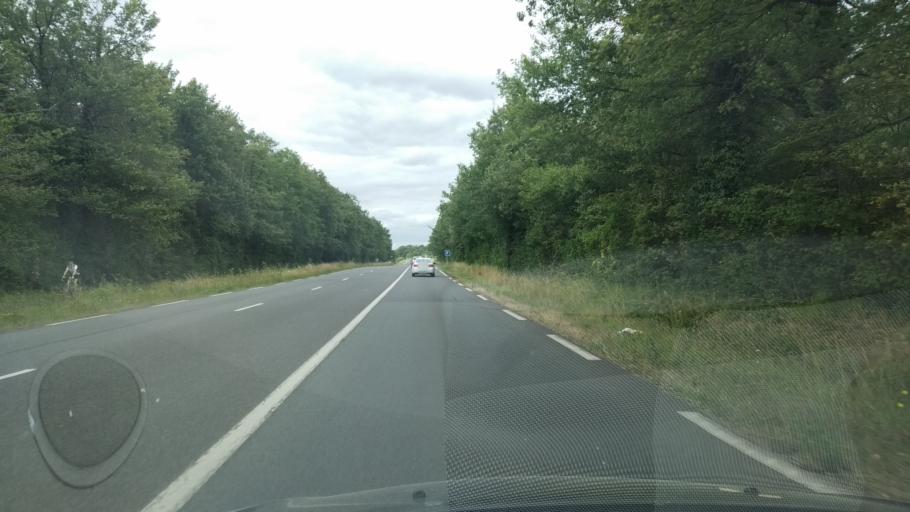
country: FR
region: Poitou-Charentes
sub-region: Departement de la Vienne
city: Smarves
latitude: 46.5256
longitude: 0.3540
